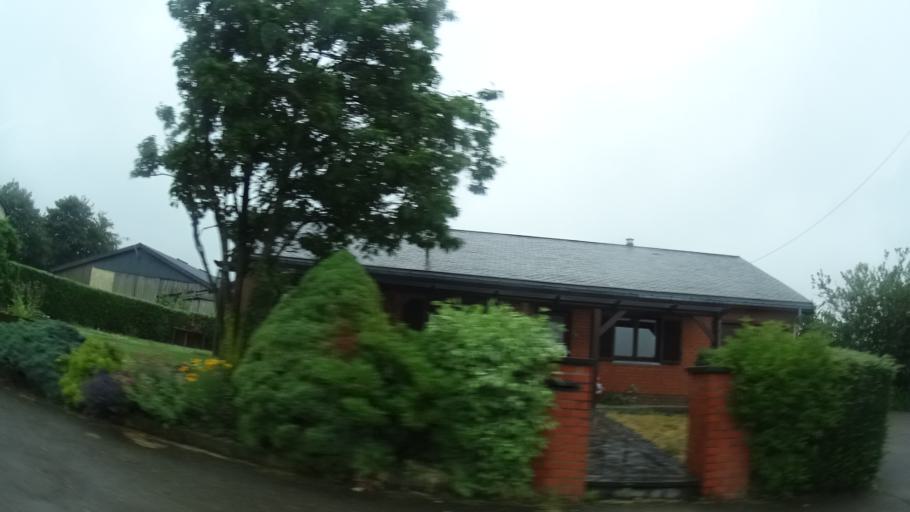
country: BE
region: Wallonia
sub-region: Province du Luxembourg
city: Bertrix
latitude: 49.8787
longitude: 5.2074
